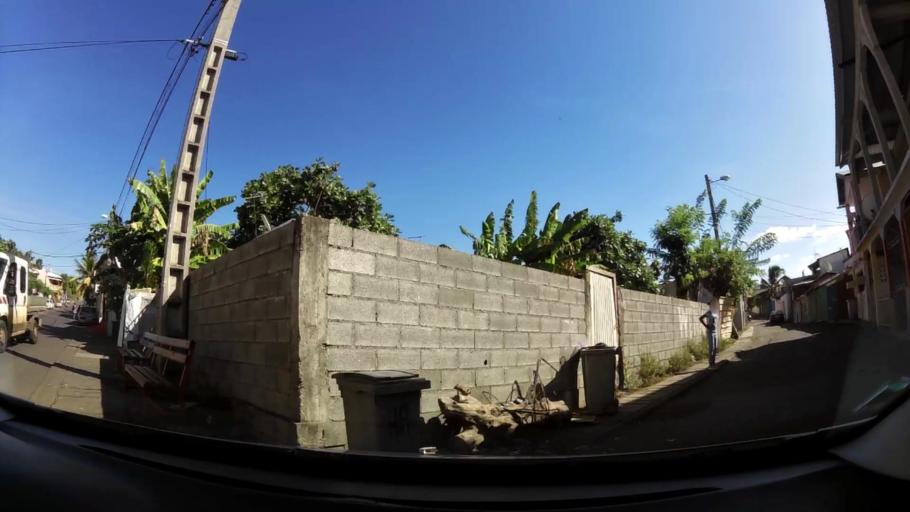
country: YT
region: Pamandzi
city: Pamandzi
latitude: -12.7896
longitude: 45.2716
